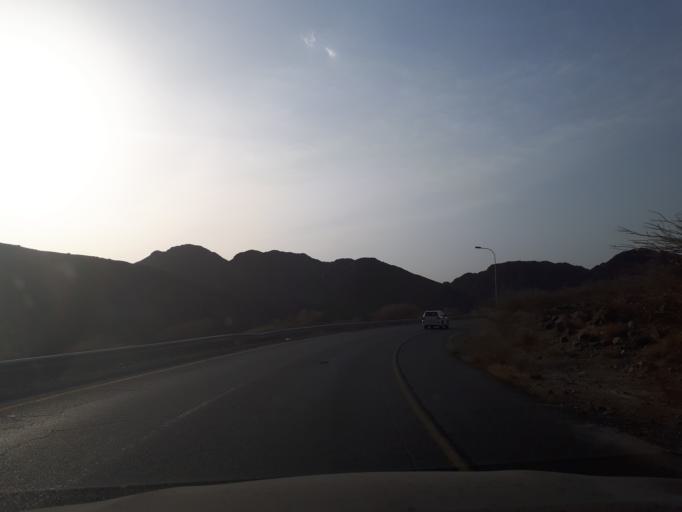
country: OM
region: Muhafazat ad Dakhiliyah
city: Sufalat Sama'il
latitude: 23.1717
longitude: 58.0962
